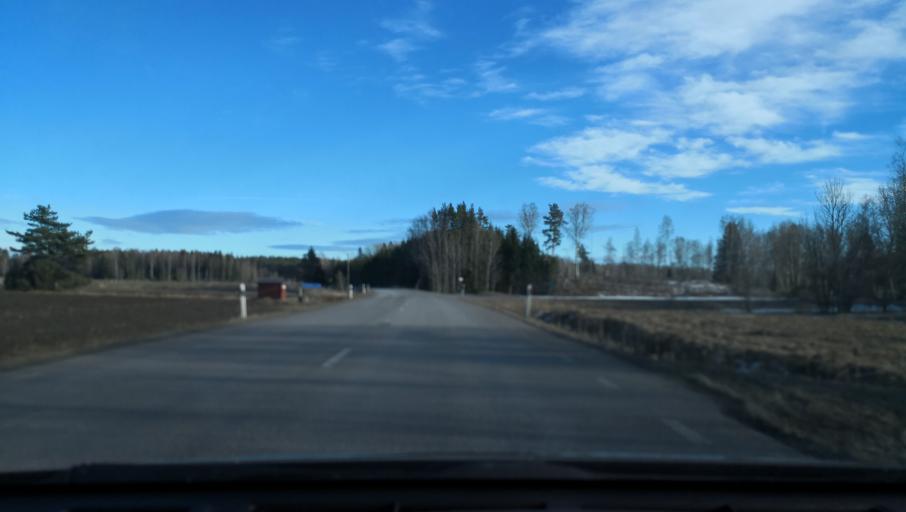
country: SE
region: Uppsala
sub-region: Osthammars Kommun
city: Osterbybruk
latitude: 60.1624
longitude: 17.9848
